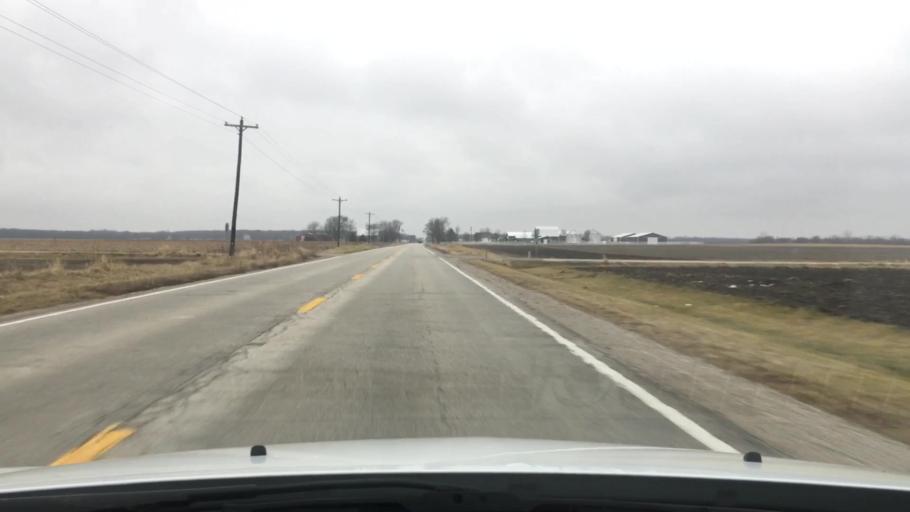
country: US
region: Illinois
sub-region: Iroquois County
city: Watseka
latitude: 40.8877
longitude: -87.8058
